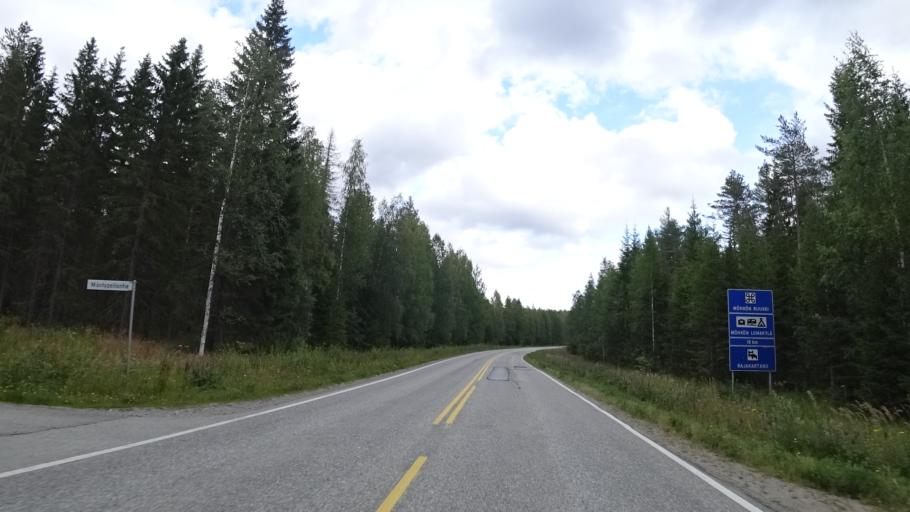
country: FI
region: North Karelia
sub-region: Joensuu
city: Ilomantsi
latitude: 62.6492
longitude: 30.9835
